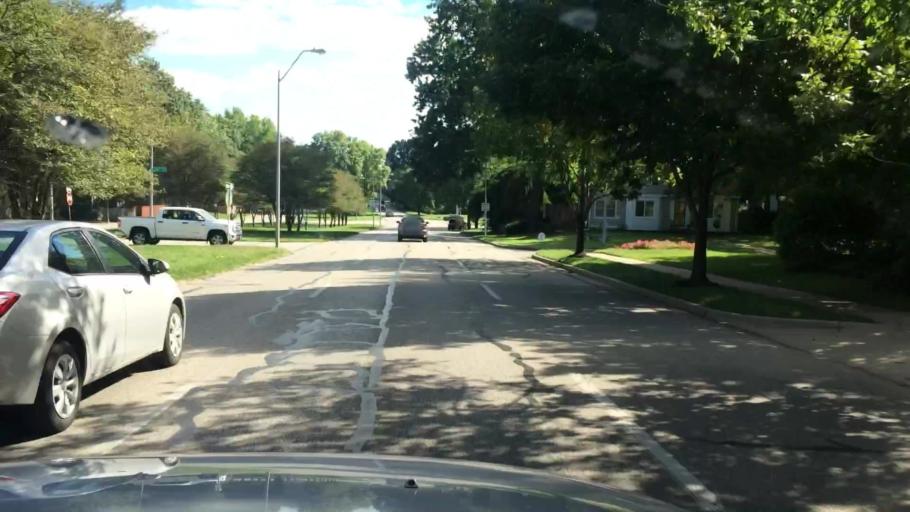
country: US
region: Kansas
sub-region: Johnson County
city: Leawood
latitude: 38.9915
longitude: -94.6039
